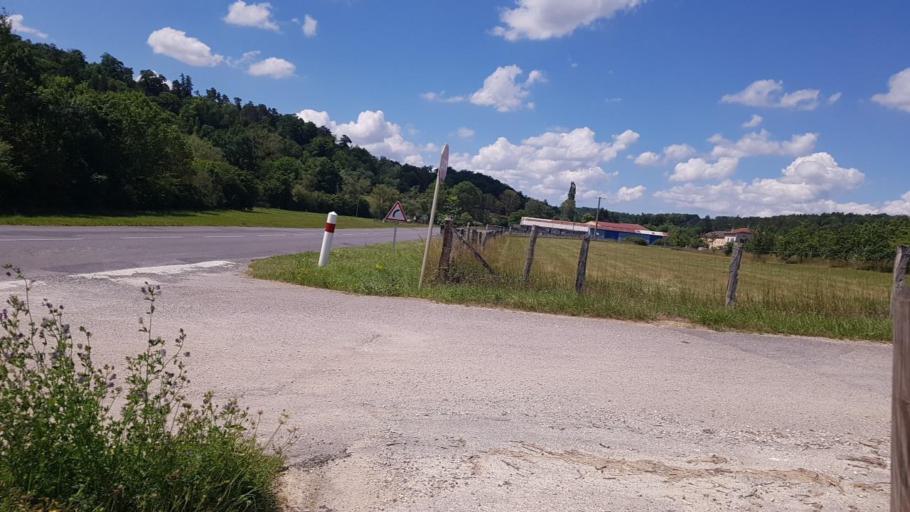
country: FR
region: Lorraine
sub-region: Departement de la Meuse
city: Vacon
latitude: 48.6683
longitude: 5.6056
